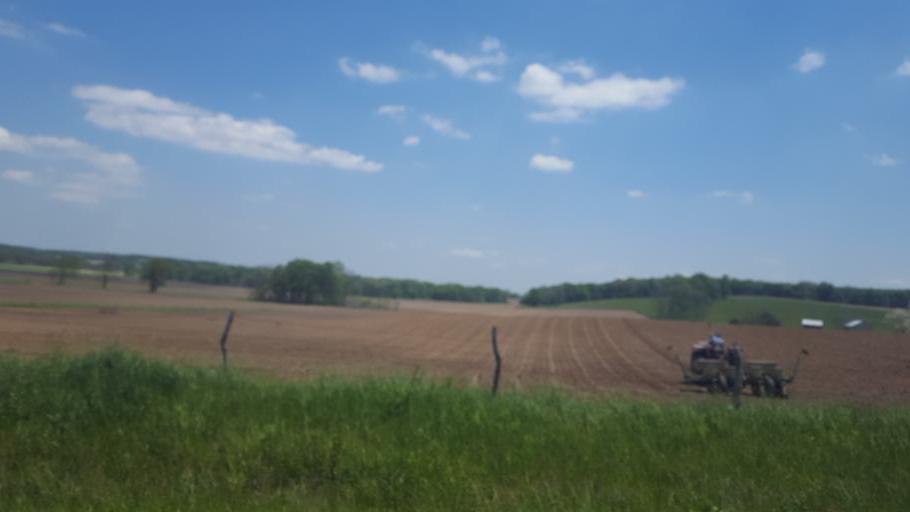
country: US
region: Ohio
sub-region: Knox County
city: Gambier
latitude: 40.3019
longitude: -82.3935
